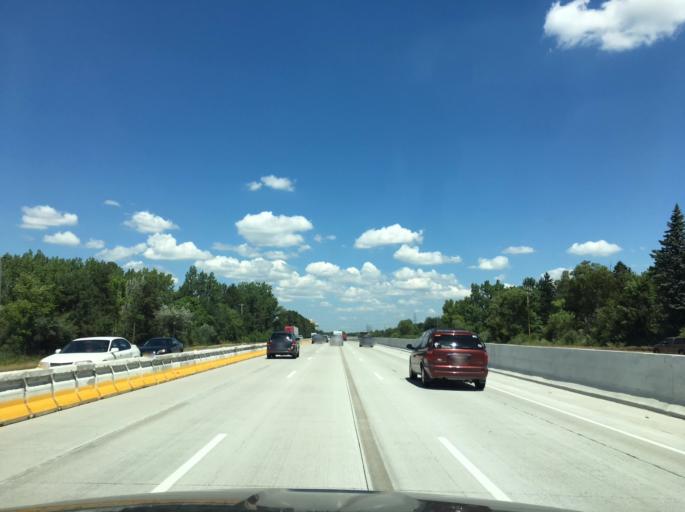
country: US
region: Michigan
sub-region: Saginaw County
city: Bridgeport
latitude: 43.3880
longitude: -83.8832
